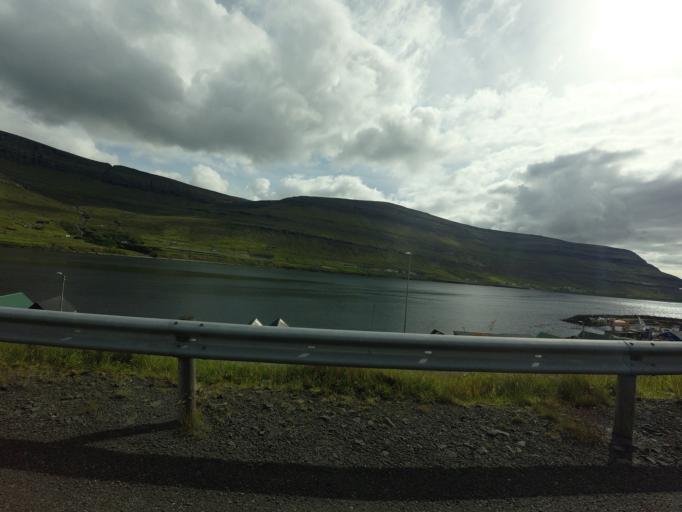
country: FO
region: Eysturoy
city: Eystur
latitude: 62.2048
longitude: -6.6727
